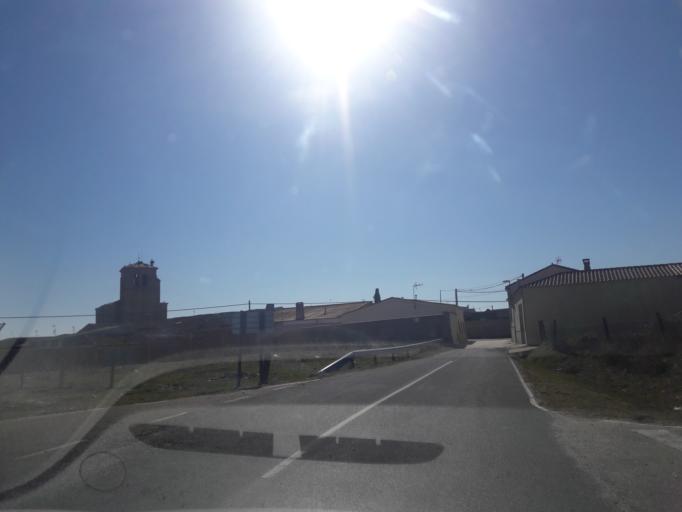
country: ES
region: Castille and Leon
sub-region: Provincia de Salamanca
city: Salmoral
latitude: 40.8020
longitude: -5.2220
